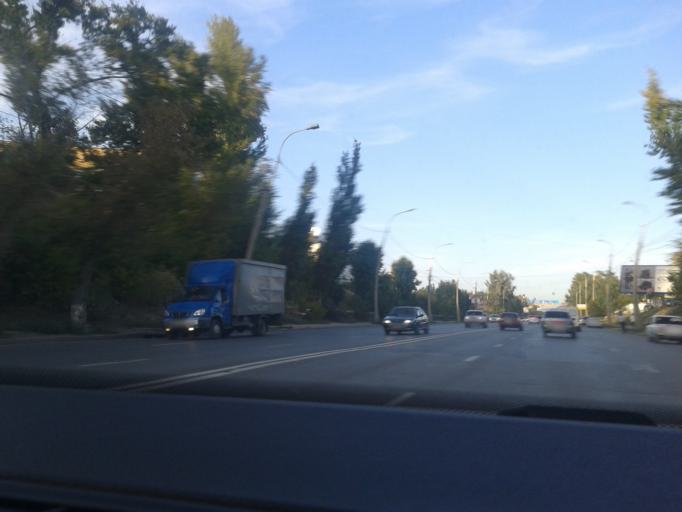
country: RU
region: Volgograd
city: Volgograd
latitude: 48.7108
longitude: 44.4929
